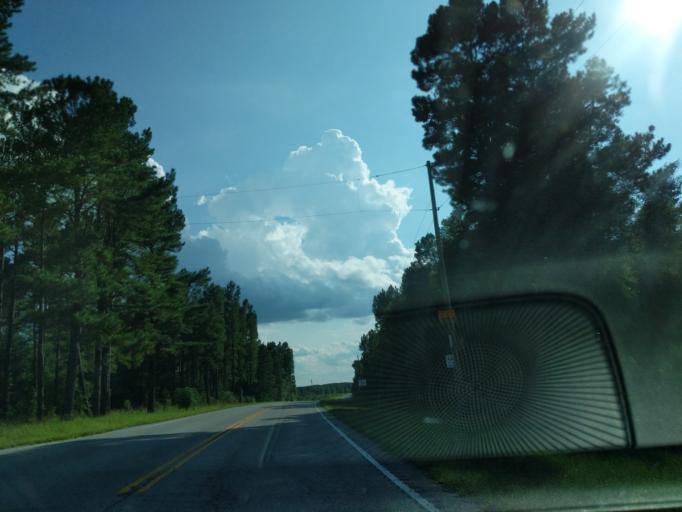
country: US
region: South Carolina
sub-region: Barnwell County
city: Williston
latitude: 33.4359
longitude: -81.3810
